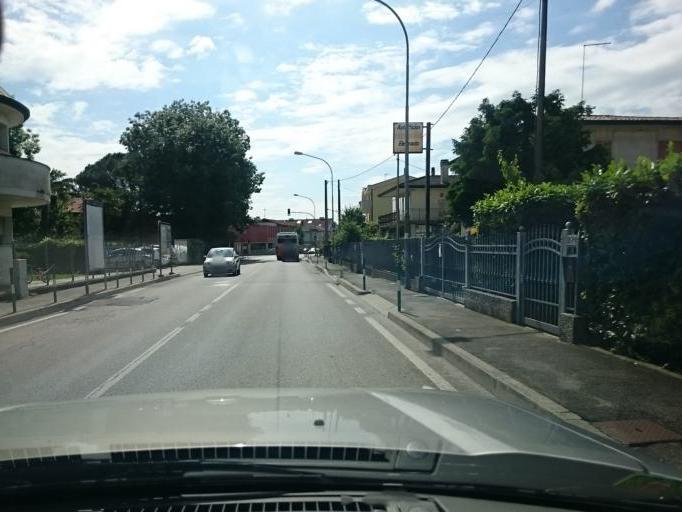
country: IT
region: Veneto
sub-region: Provincia di Padova
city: Sarmeola
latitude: 45.4319
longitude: 11.8419
